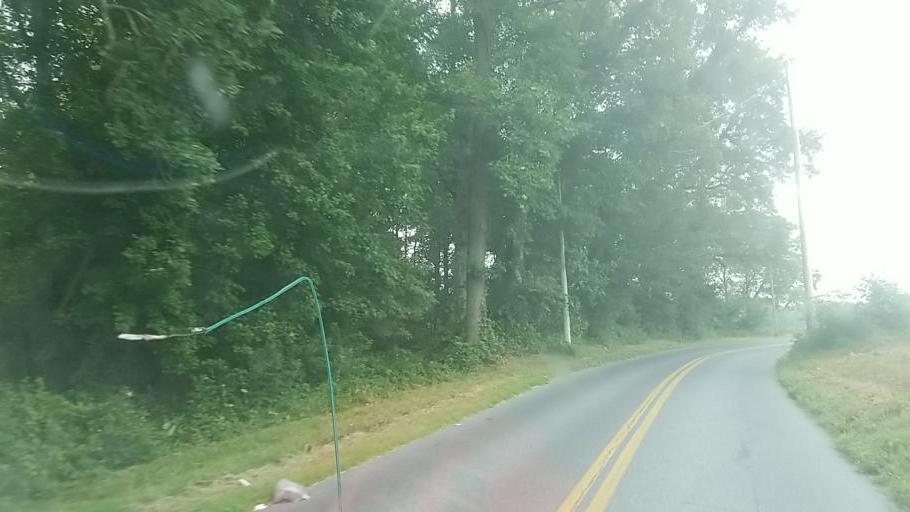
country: US
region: Delaware
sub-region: Sussex County
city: Selbyville
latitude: 38.4394
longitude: -75.1931
